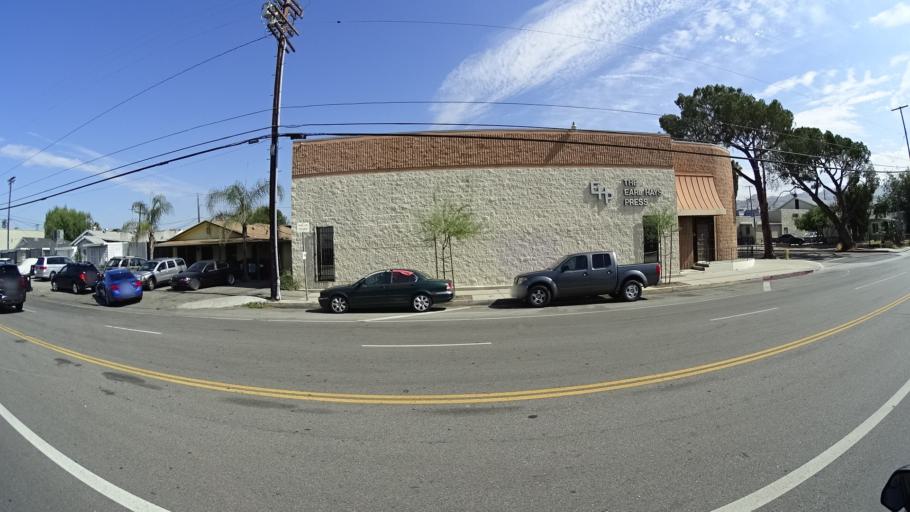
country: US
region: California
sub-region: Los Angeles County
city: North Hollywood
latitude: 34.2011
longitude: -118.3636
